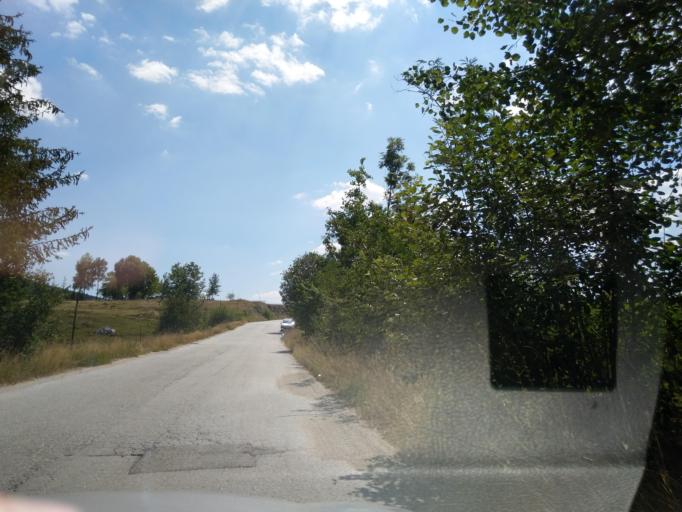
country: RS
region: Central Serbia
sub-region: Zlatiborski Okrug
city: Nova Varos
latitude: 43.4321
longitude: 19.9499
